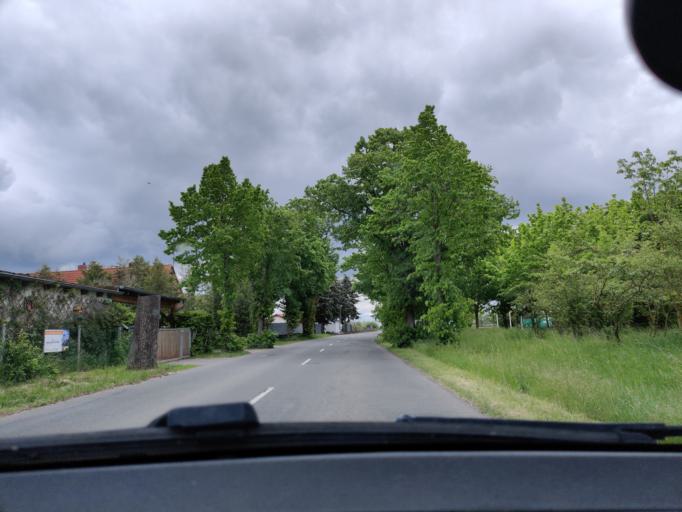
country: DE
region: Saxony-Anhalt
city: Schonebeck
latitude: 51.9736
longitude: 11.7786
